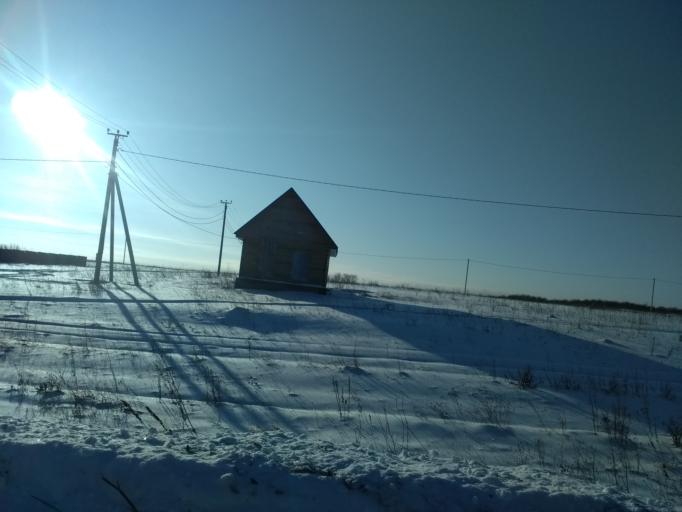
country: RU
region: Bashkortostan
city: Iglino
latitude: 54.6850
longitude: 56.6026
